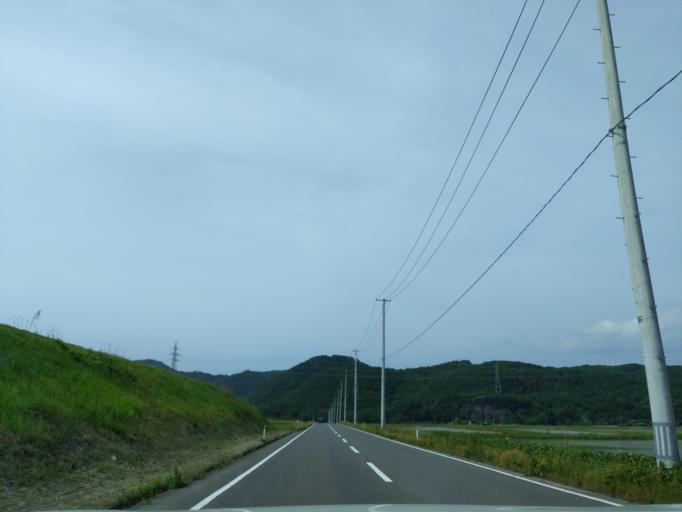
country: JP
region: Fukushima
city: Motomiya
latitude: 37.4719
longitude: 140.3160
